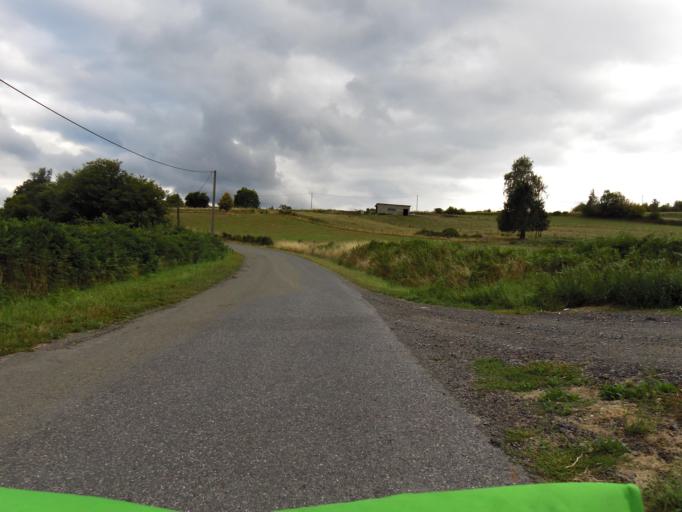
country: BE
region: Wallonia
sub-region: Province de Namur
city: Bievre
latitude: 49.8741
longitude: 4.9810
